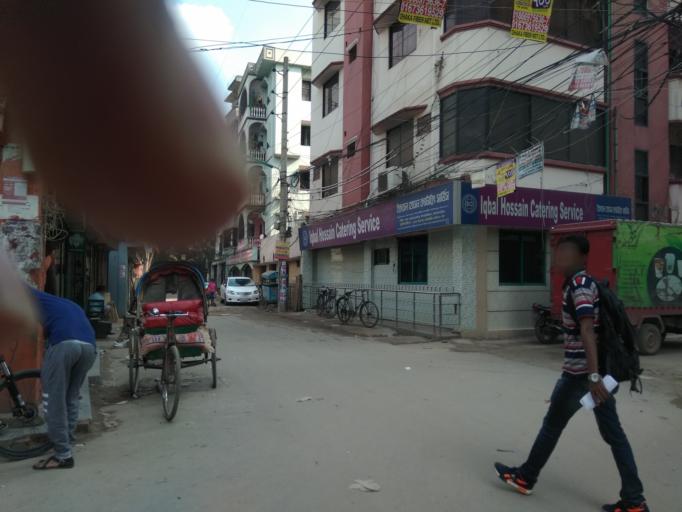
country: BD
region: Dhaka
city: Azimpur
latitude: 23.7646
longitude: 90.3533
